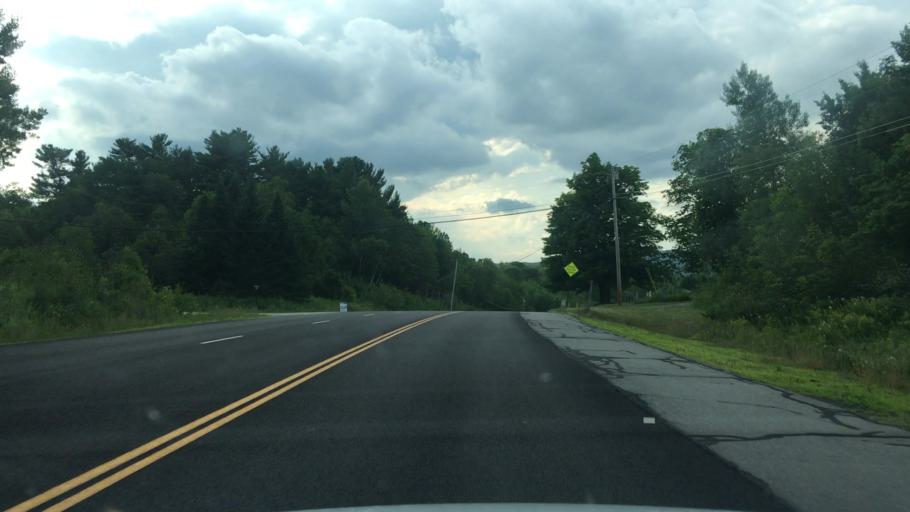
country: US
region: Maine
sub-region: Waldo County
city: Palermo
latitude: 44.3700
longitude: -69.3914
